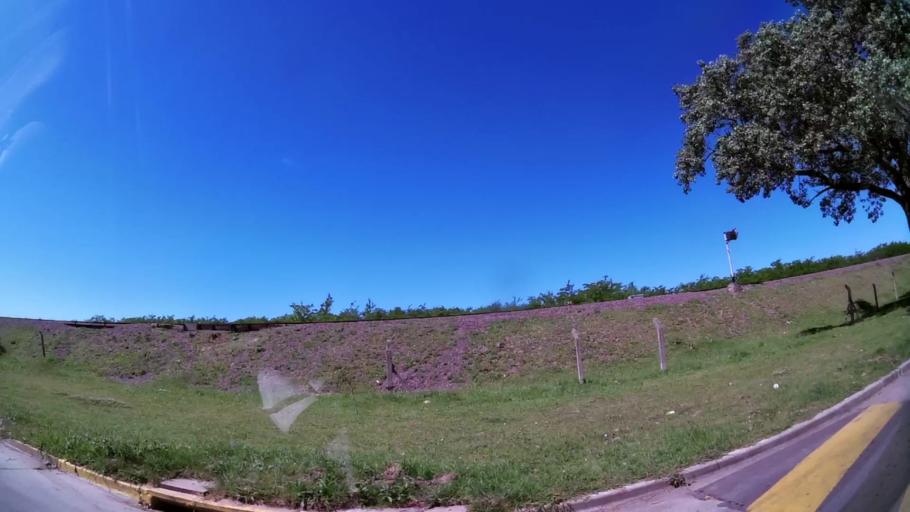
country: AR
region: Buenos Aires
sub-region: Partido de Tigre
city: Tigre
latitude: -34.5045
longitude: -58.6101
